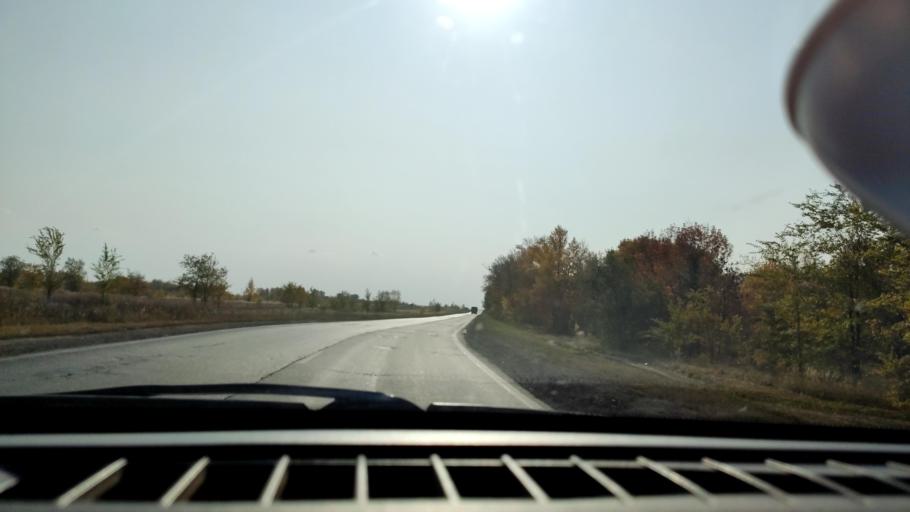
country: RU
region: Samara
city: Smyshlyayevka
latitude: 53.1206
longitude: 50.3667
